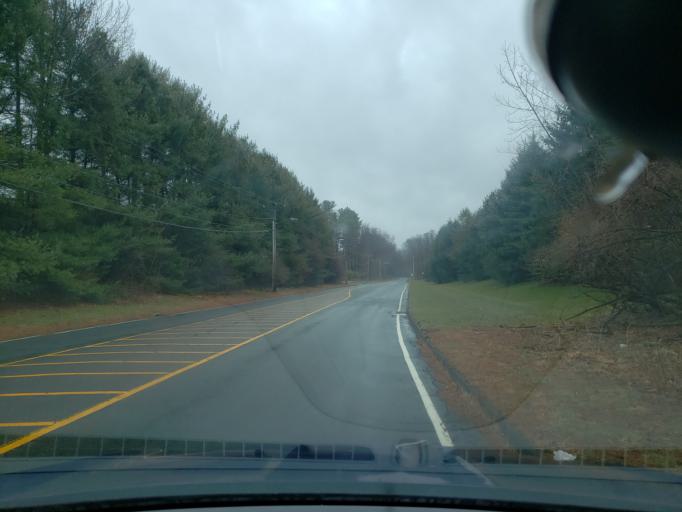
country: US
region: Connecticut
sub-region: Hartford County
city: Windsor
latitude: 41.8829
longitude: -72.6855
